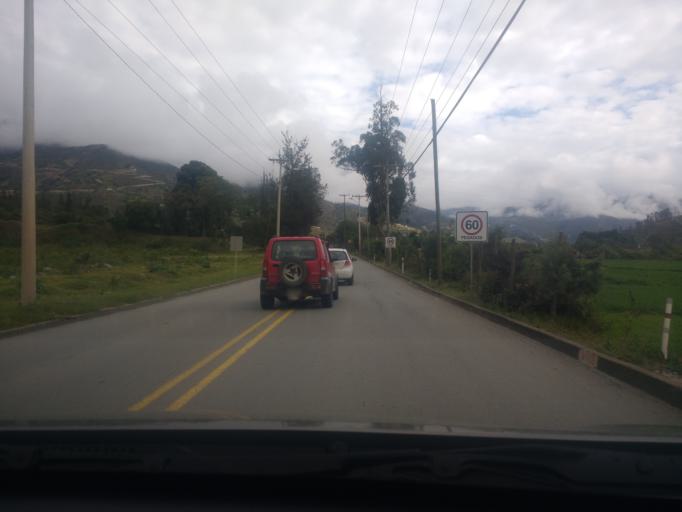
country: EC
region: Azuay
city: La Union
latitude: -2.8195
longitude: -78.7726
